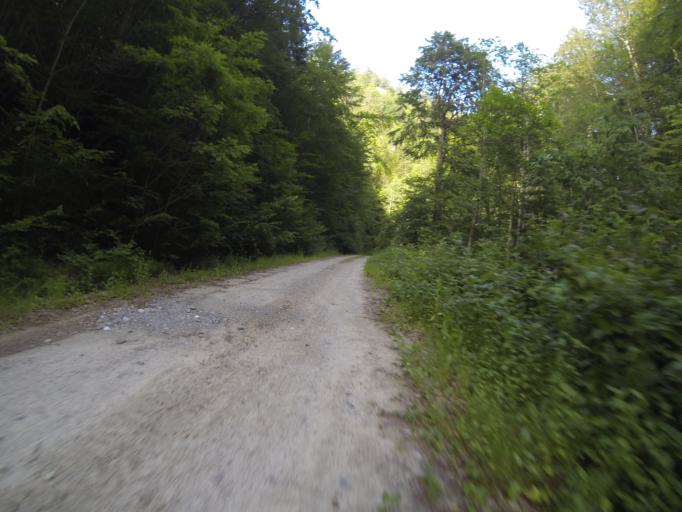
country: RO
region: Valcea
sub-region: Oras Baile Olanesti
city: Baile Olanesti
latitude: 45.2445
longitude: 24.1835
